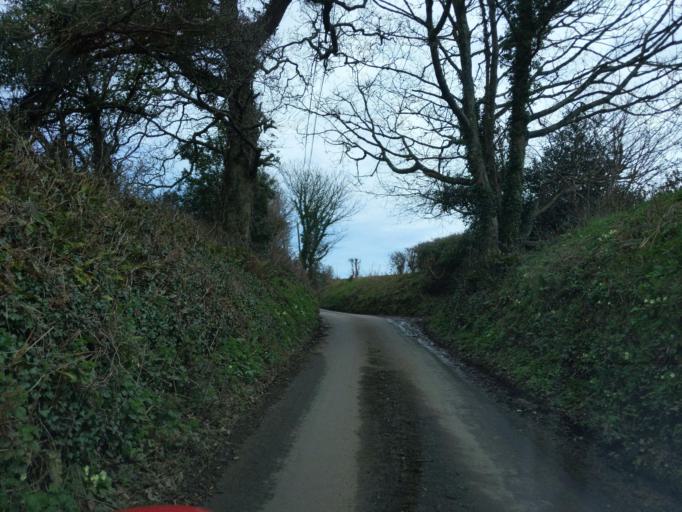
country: GB
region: England
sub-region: Devon
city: Yealmpton
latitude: 50.3630
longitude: -4.0075
